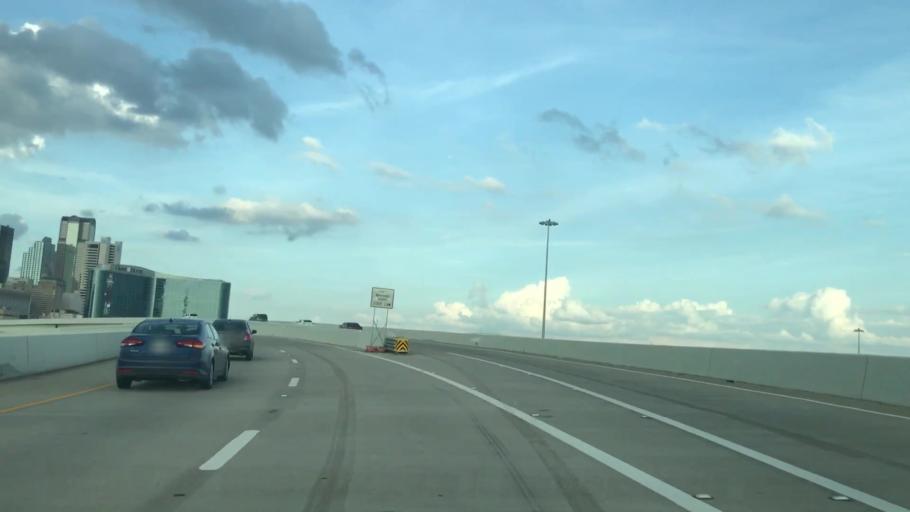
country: US
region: Texas
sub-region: Dallas County
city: Dallas
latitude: 32.7708
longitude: -96.8122
